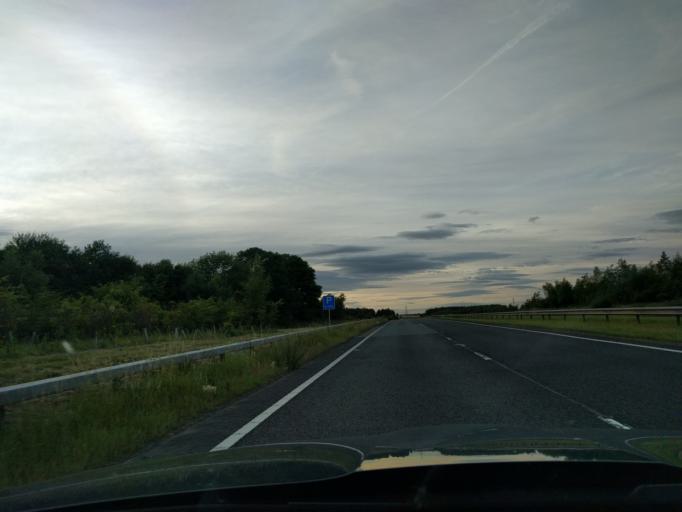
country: GB
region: England
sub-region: Northumberland
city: Stannington
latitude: 55.1148
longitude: -1.6675
